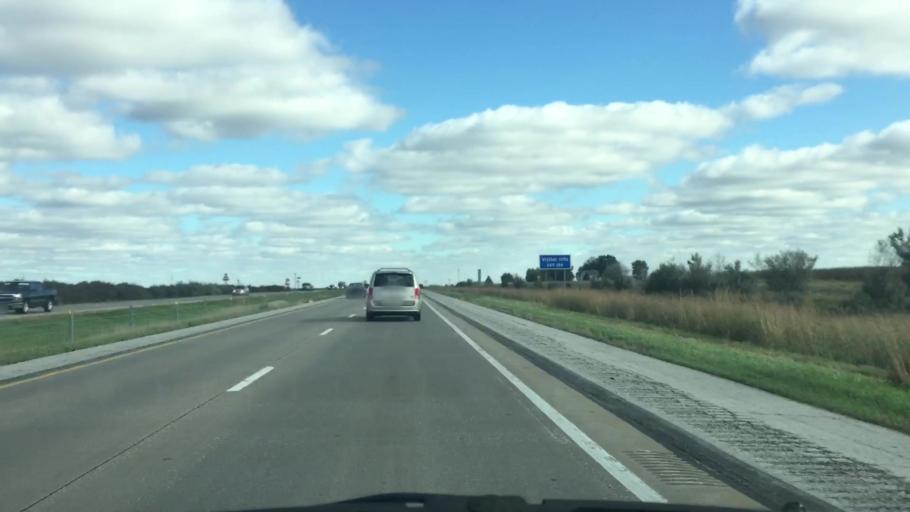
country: US
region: Iowa
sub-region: Scott County
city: Walcott
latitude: 41.6232
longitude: -90.8082
